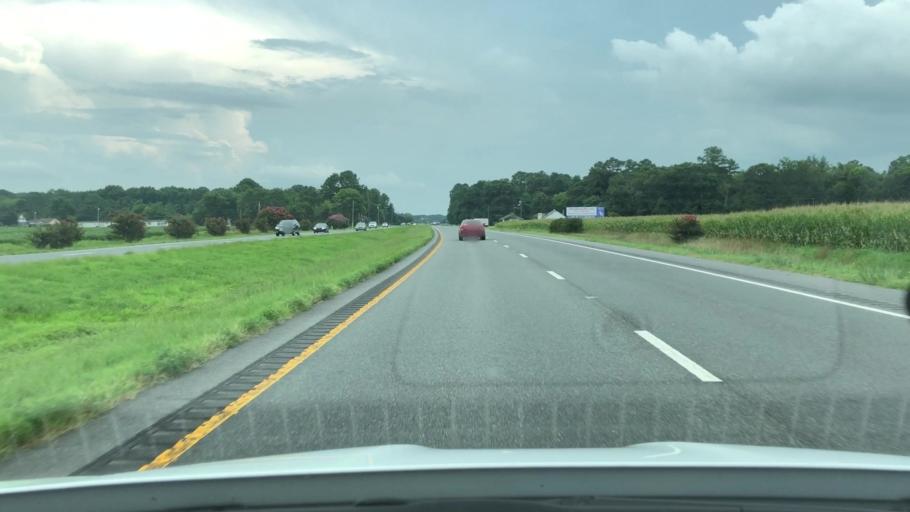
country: US
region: Virginia
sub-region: Northampton County
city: Eastville
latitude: 37.3958
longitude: -75.9134
